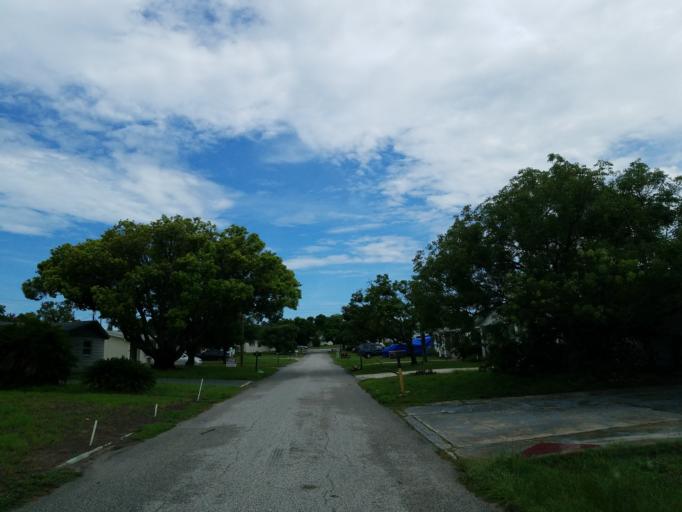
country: US
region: Florida
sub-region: Pasco County
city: Beacon Square
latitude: 28.2083
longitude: -82.7445
